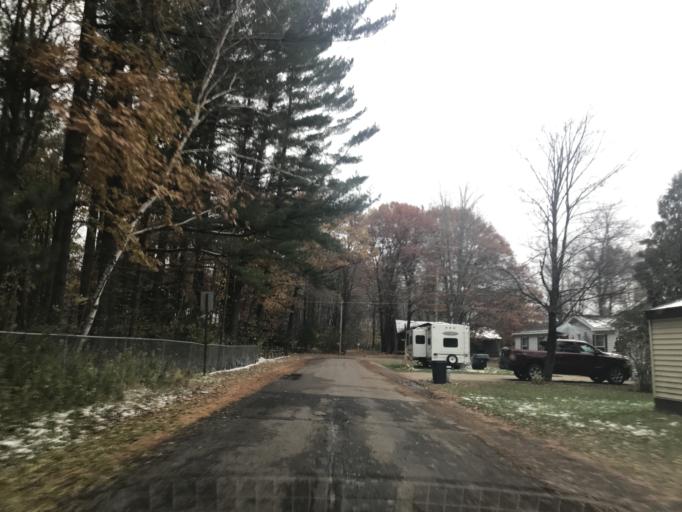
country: US
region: Wisconsin
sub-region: Marinette County
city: Marinette
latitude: 45.0965
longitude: -87.6548
